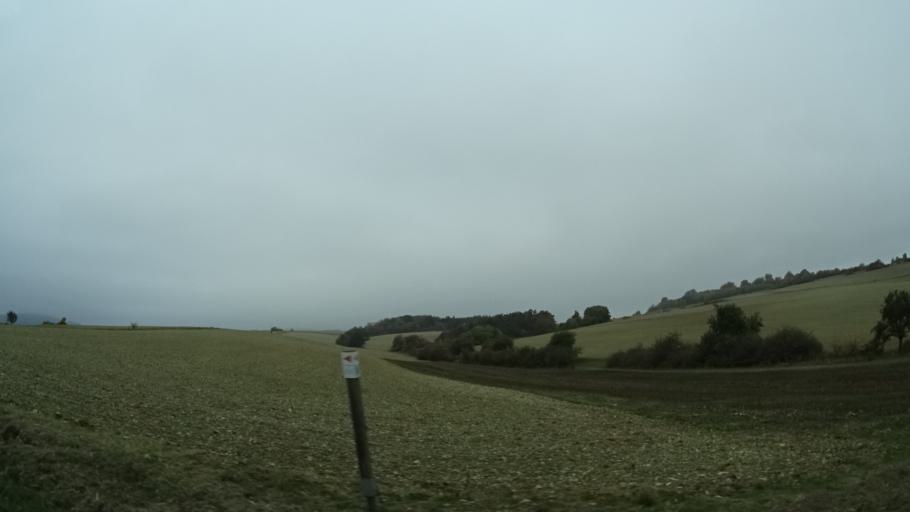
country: DE
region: Thuringia
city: Erbenhausen
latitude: 50.5928
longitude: 10.1493
